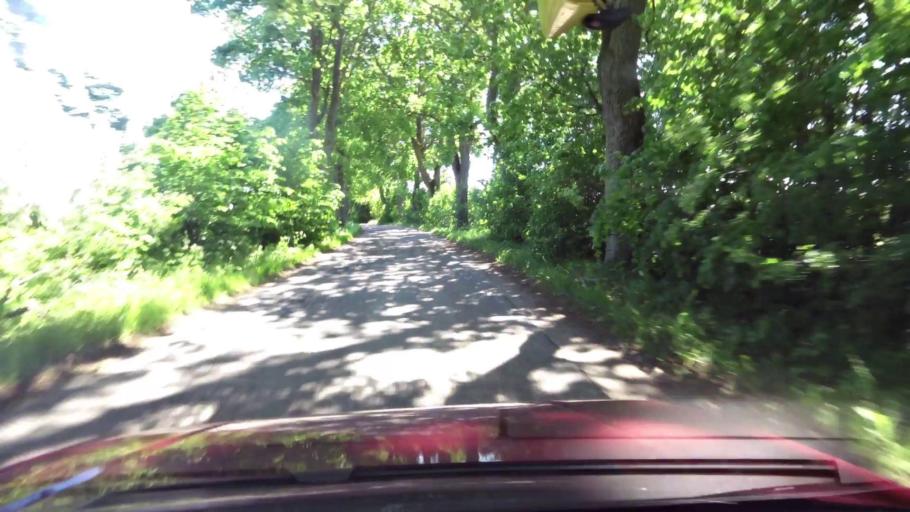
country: PL
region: West Pomeranian Voivodeship
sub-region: Powiat koszalinski
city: Bobolice
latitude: 54.0144
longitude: 16.6542
